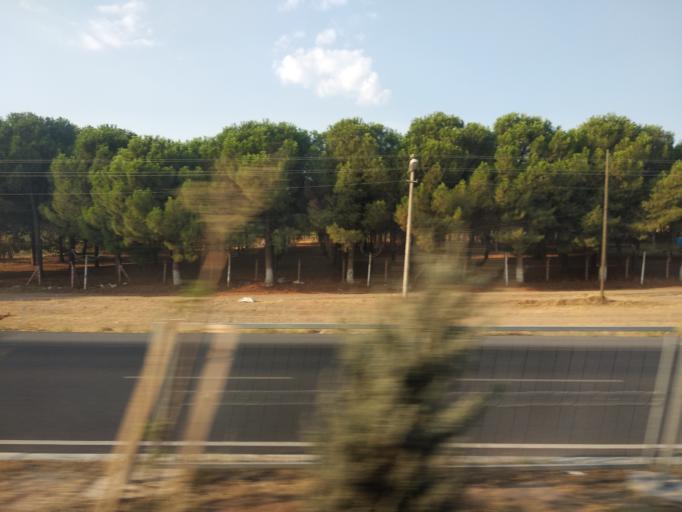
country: TR
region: Manisa
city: Ahmetli
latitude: 38.5048
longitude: 28.0054
